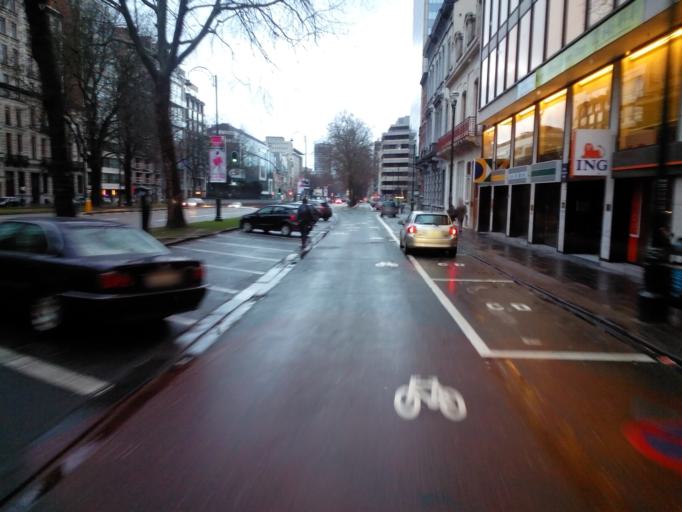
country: BE
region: Brussels Capital
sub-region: Bruxelles-Capitale
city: Brussels
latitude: 50.8220
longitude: 4.3698
